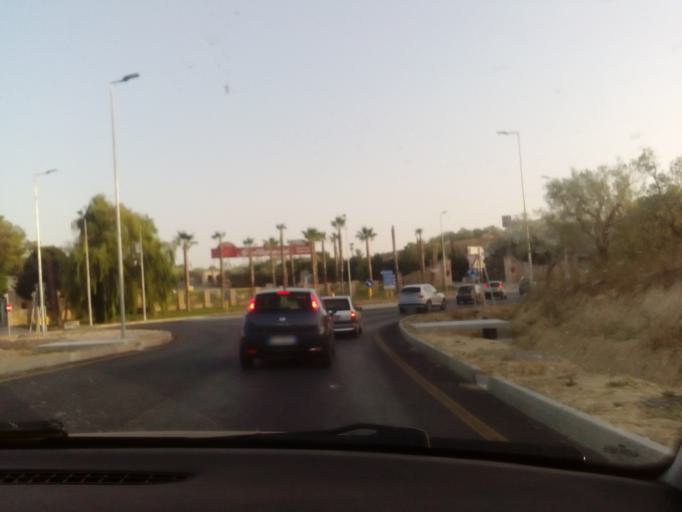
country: IT
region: Apulia
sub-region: Provincia di Bari
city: Altamura
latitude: 40.8429
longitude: 16.5750
